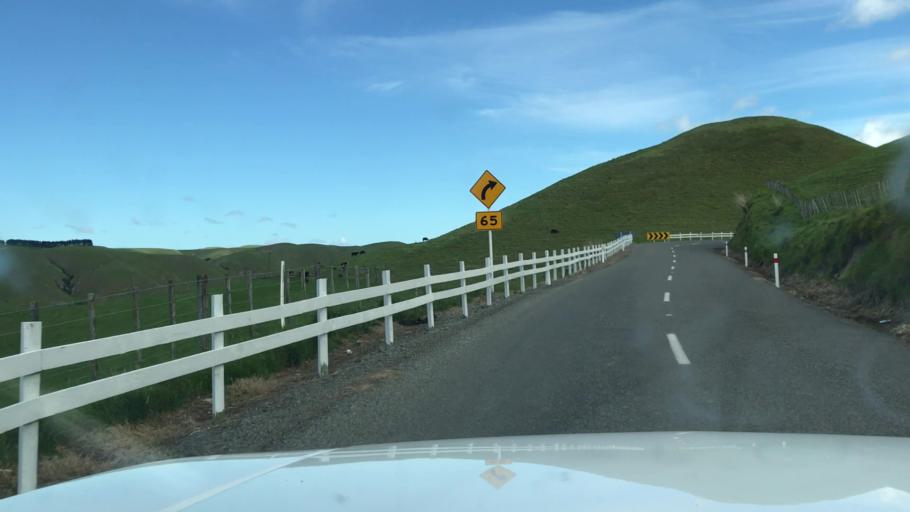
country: NZ
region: Hawke's Bay
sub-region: Hastings District
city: Hastings
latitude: -39.8162
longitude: 176.7474
